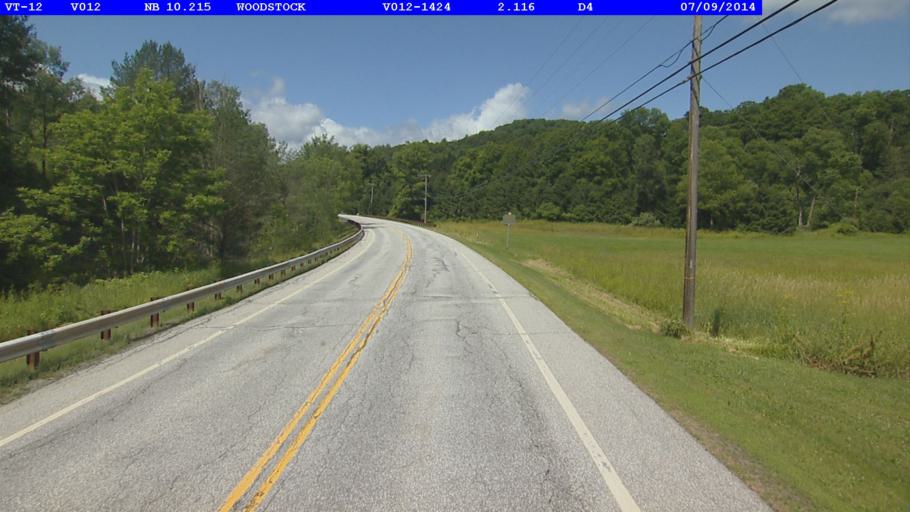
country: US
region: Vermont
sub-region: Windsor County
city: Woodstock
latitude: 43.6472
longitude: -72.5395
